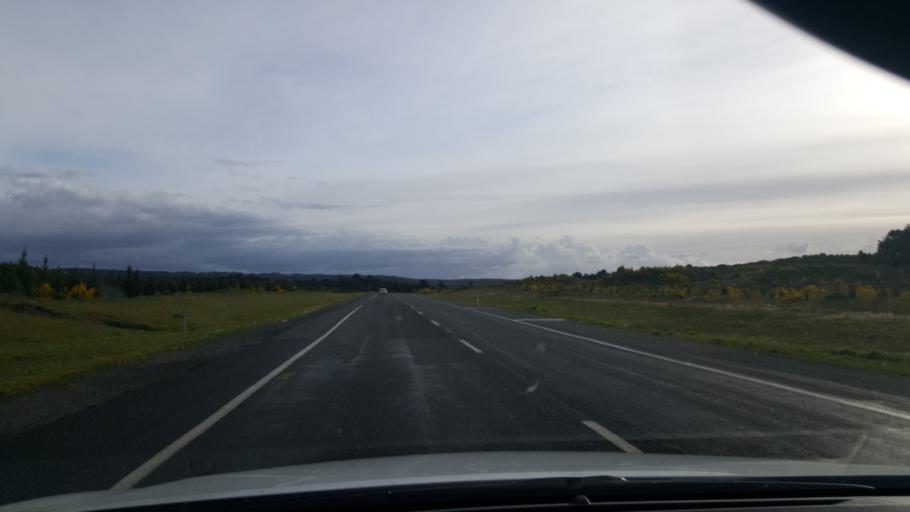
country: NZ
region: Waikato
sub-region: Taupo District
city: Taupo
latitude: -38.8486
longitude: 176.0565
